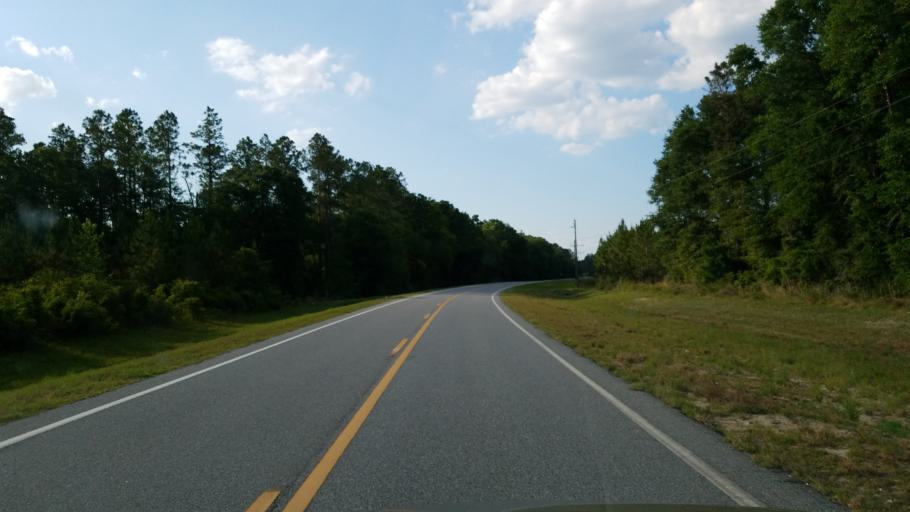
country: US
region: Georgia
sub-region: Echols County
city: Statenville
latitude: 30.7649
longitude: -83.0559
